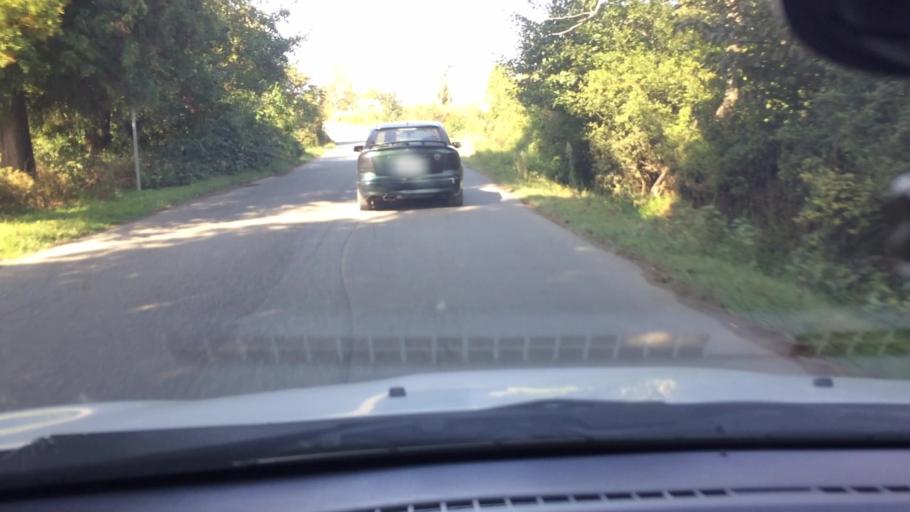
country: GE
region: Ajaria
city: Kobuleti
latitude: 41.8052
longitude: 41.7986
